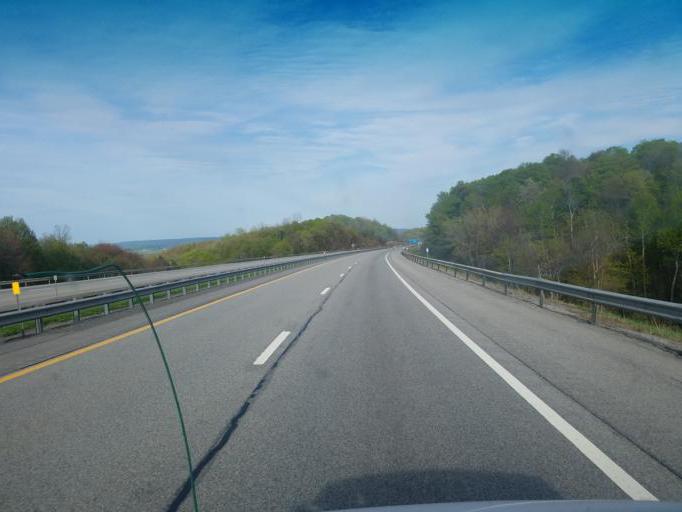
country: US
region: New York
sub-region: Herkimer County
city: Little Falls
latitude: 43.0116
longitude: -74.8538
